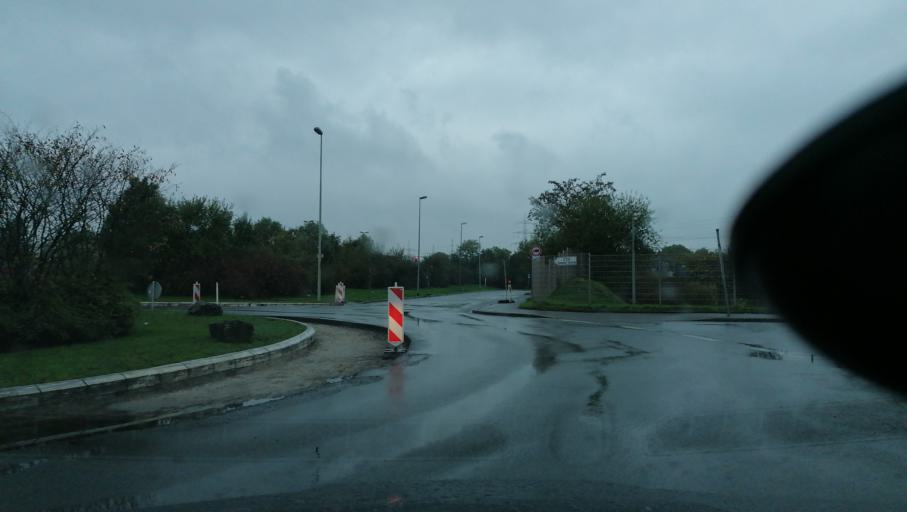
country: DE
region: North Rhine-Westphalia
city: Herten
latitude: 51.5485
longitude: 7.1519
